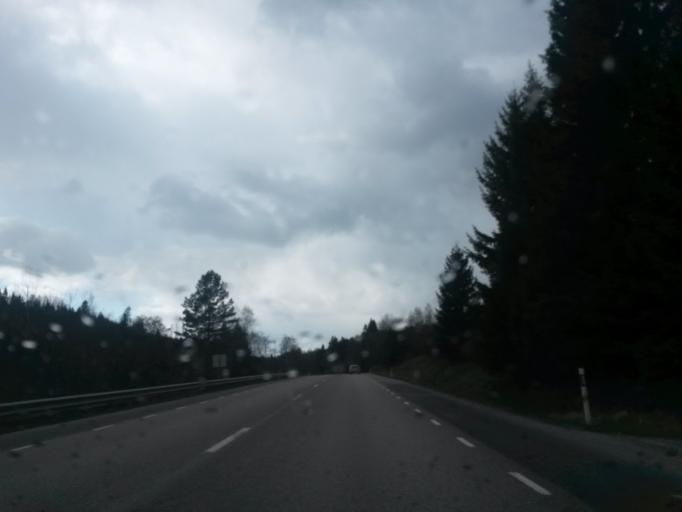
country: SE
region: Vaestra Goetaland
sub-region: Skovde Kommun
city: Skoevde
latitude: 58.3925
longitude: 13.7803
